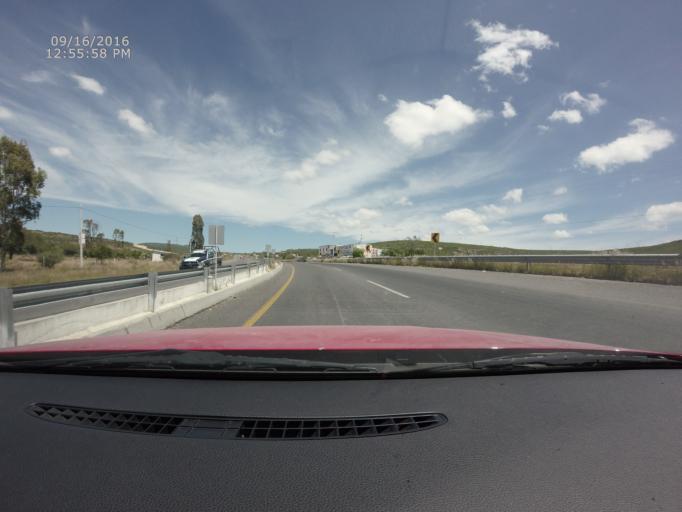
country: MX
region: Queretaro
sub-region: Colon
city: Purisima de Cubos (La Purisima)
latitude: 20.6465
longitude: -100.0991
